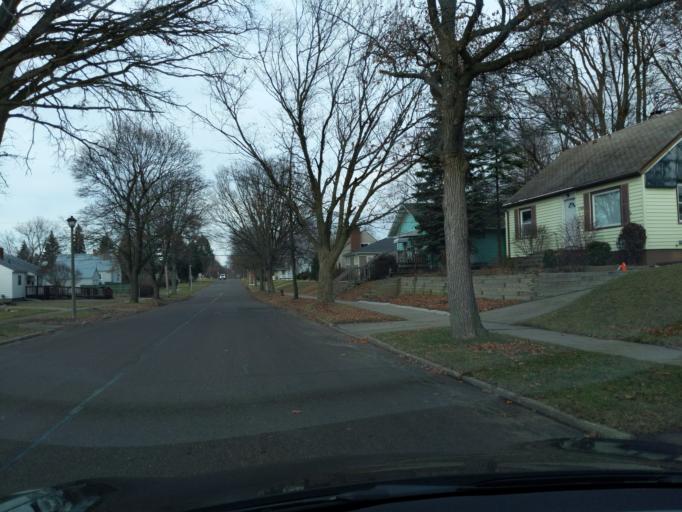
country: US
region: Michigan
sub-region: Ingham County
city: Lansing
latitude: 42.7139
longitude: -84.5723
